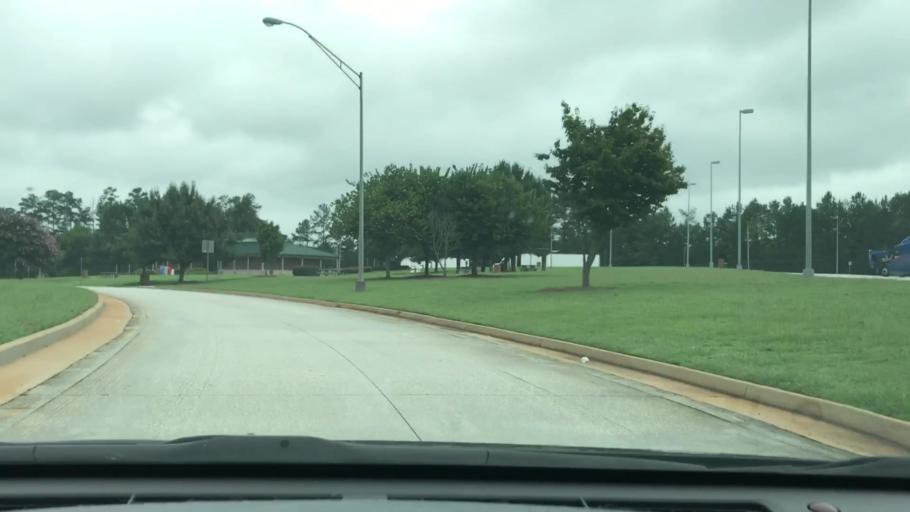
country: US
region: Georgia
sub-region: Morgan County
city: Madison
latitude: 33.5792
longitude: -83.5763
